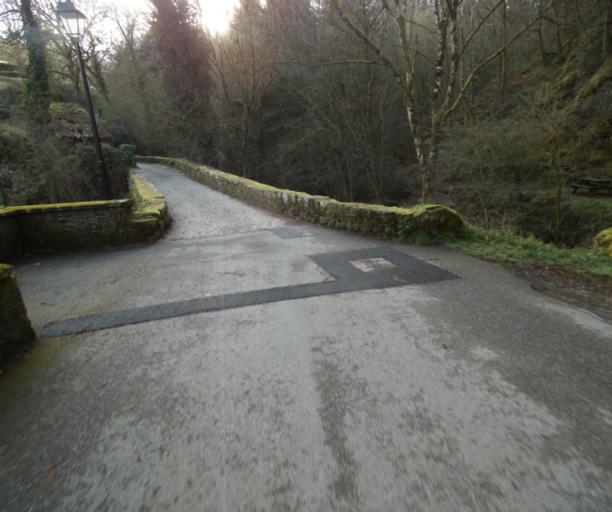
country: FR
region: Limousin
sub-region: Departement de la Correze
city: Correze
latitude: 45.2980
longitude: 1.8504
